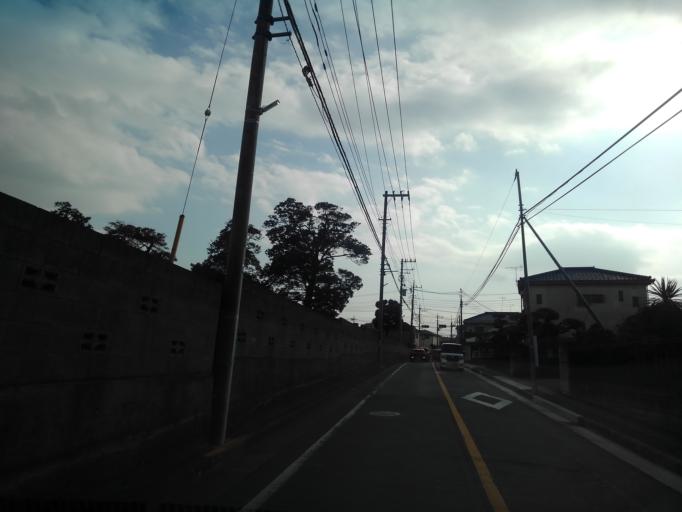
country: JP
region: Tokyo
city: Higashimurayama-shi
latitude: 35.7721
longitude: 139.4735
